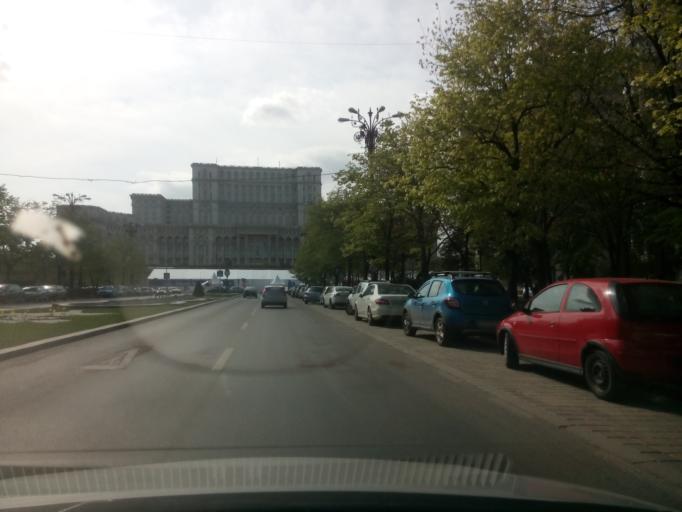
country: RO
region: Bucuresti
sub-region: Municipiul Bucuresti
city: Bucuresti
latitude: 44.4273
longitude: 26.0942
